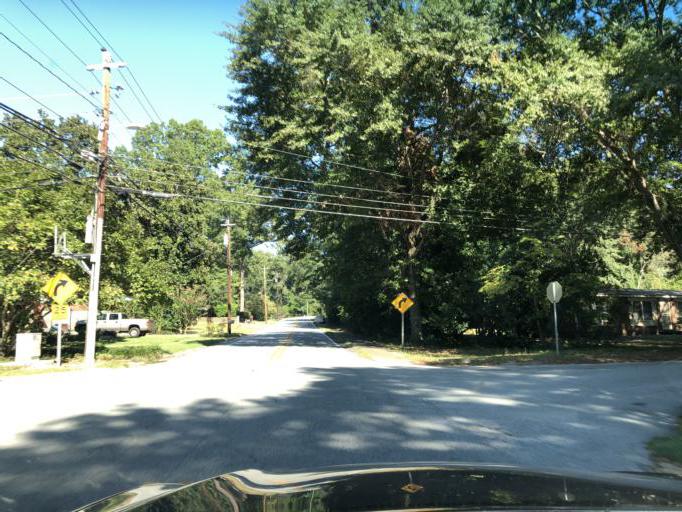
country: US
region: Georgia
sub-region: Muscogee County
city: Columbus
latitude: 32.5068
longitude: -84.9165
